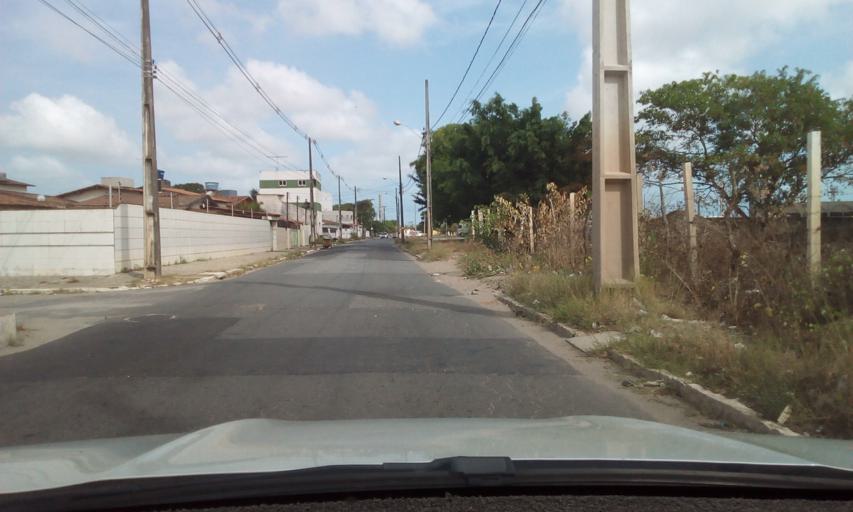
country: BR
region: Paraiba
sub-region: Joao Pessoa
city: Joao Pessoa
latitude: -7.1647
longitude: -34.8757
